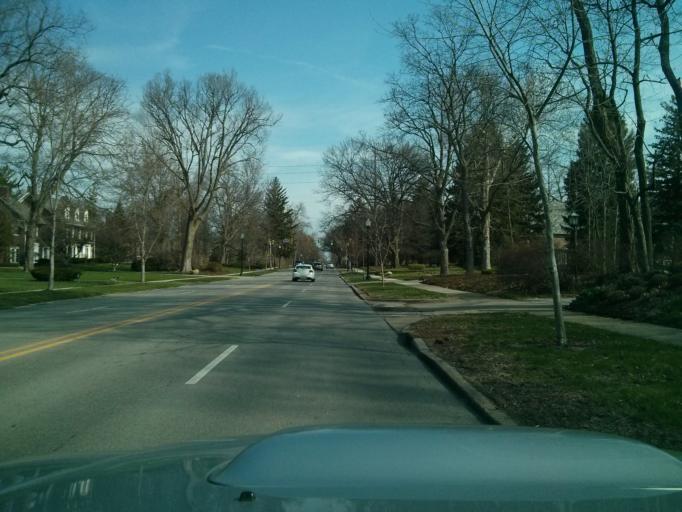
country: US
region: Indiana
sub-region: Marion County
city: Broad Ripple
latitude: 39.8413
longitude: -86.1569
